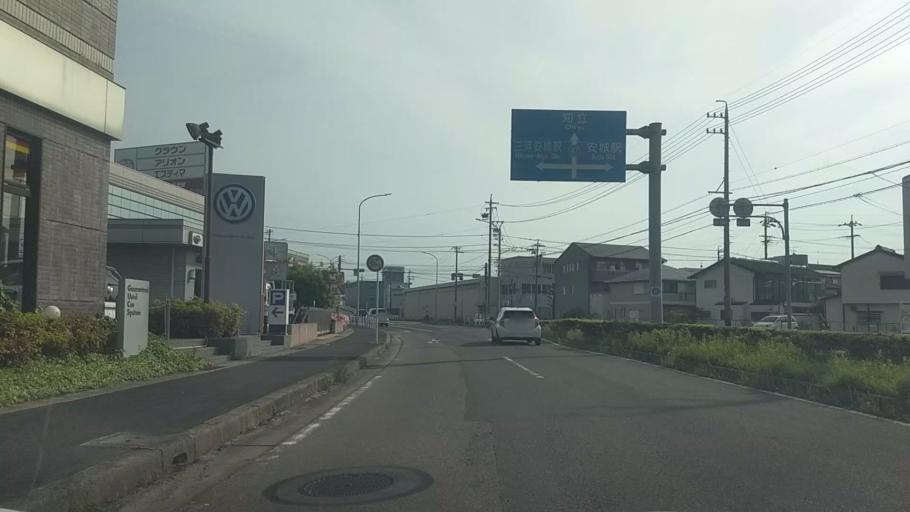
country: JP
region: Aichi
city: Anjo
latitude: 34.9637
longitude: 137.0709
